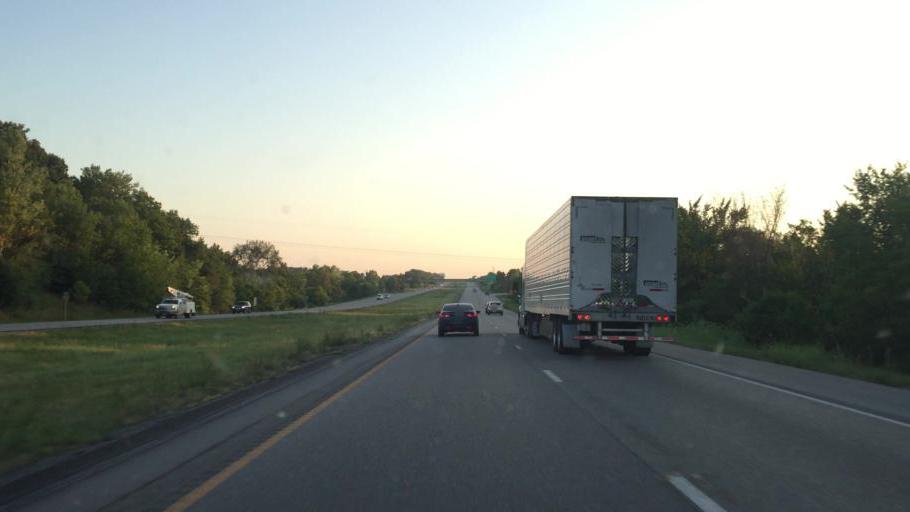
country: US
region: Missouri
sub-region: Clay County
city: Pleasant Valley
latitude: 39.2798
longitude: -94.5101
